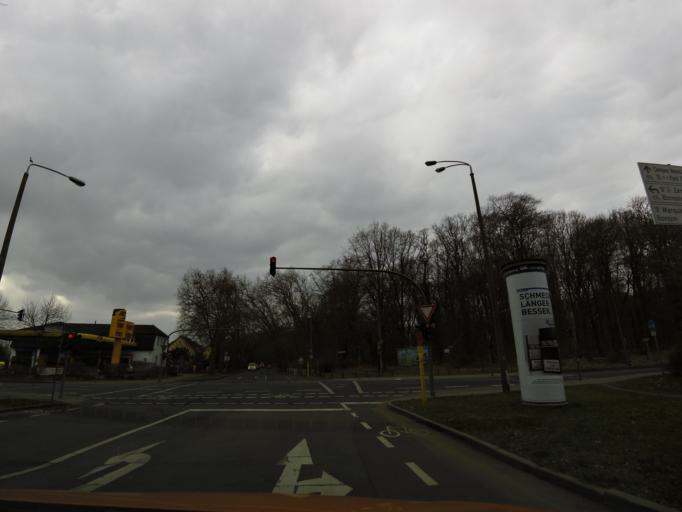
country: DE
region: Brandenburg
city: Potsdam
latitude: 52.4173
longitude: 13.0199
